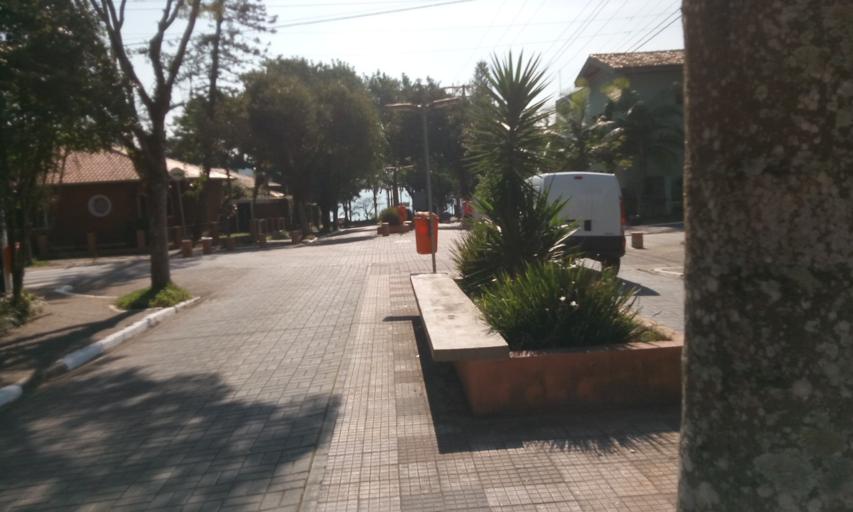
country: BR
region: Sao Paulo
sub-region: Sao Bernardo Do Campo
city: Sao Bernardo do Campo
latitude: -23.7775
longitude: -46.5317
